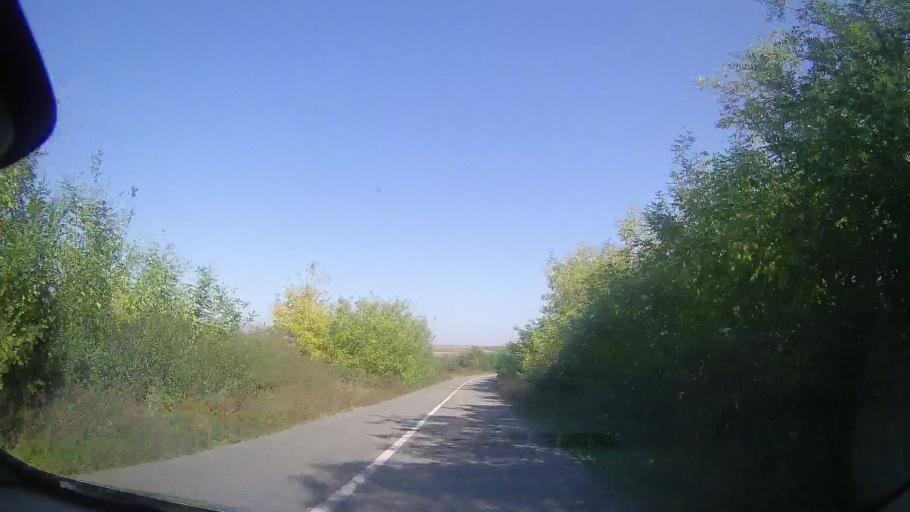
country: RO
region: Timis
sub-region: Comuna Balint
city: Balint
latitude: 45.8333
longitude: 21.8553
